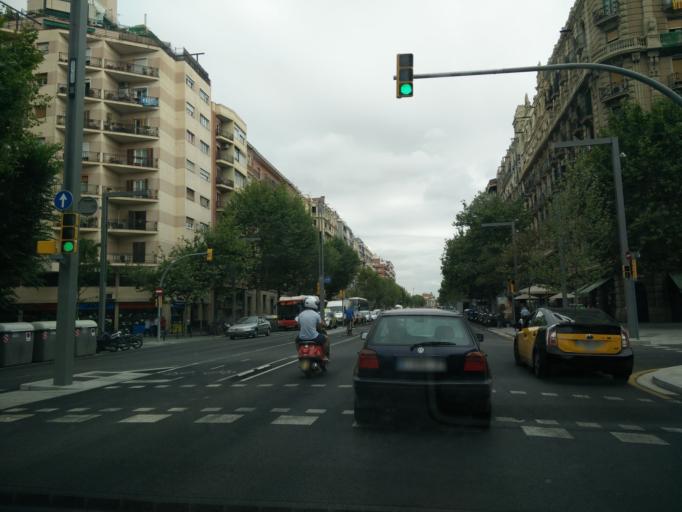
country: ES
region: Catalonia
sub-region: Provincia de Barcelona
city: Sants-Montjuic
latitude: 41.3751
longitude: 2.1589
